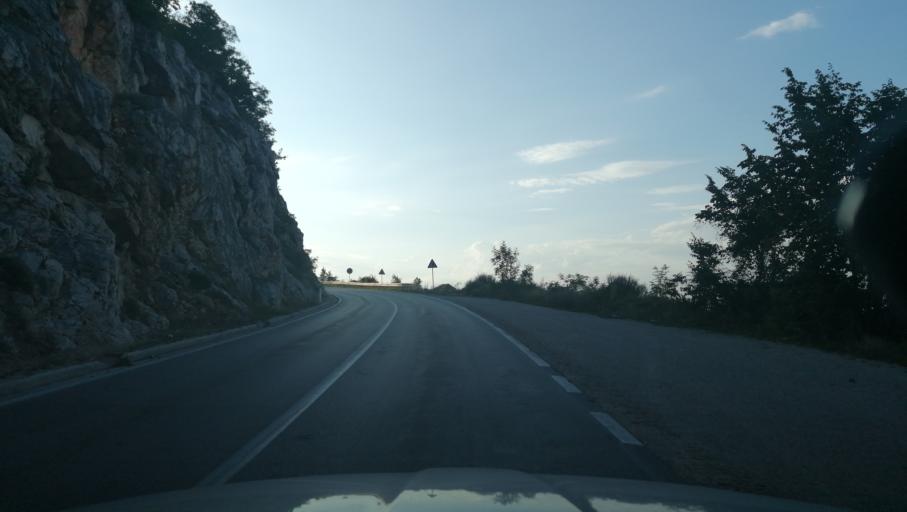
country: BA
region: Federation of Bosnia and Herzegovina
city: Prozor
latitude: 43.8377
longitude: 17.5882
